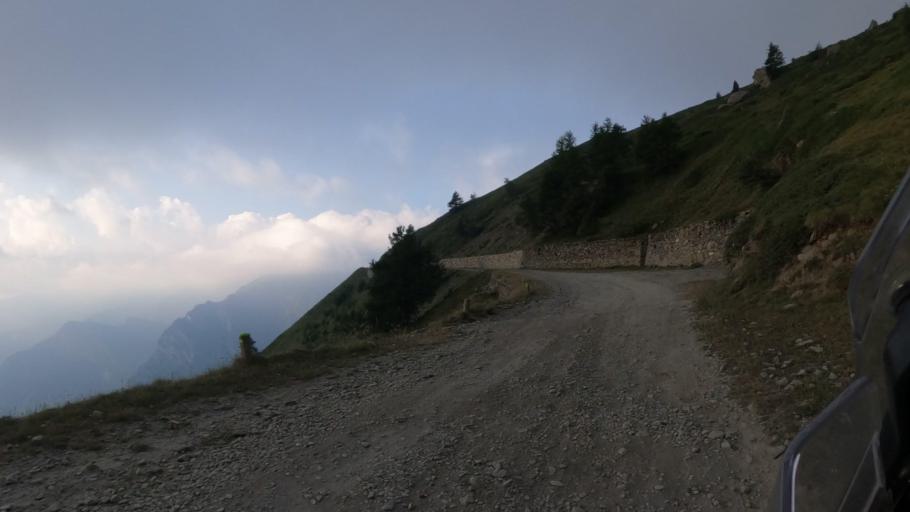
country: IT
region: Piedmont
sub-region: Provincia di Torino
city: Usseaux
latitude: 45.0612
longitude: 7.0037
